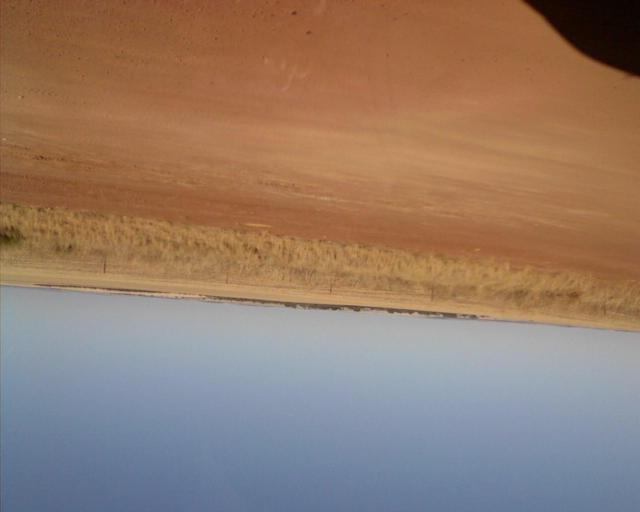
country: AU
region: Western Australia
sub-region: Moora
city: Moora
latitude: -30.2613
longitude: 116.3836
